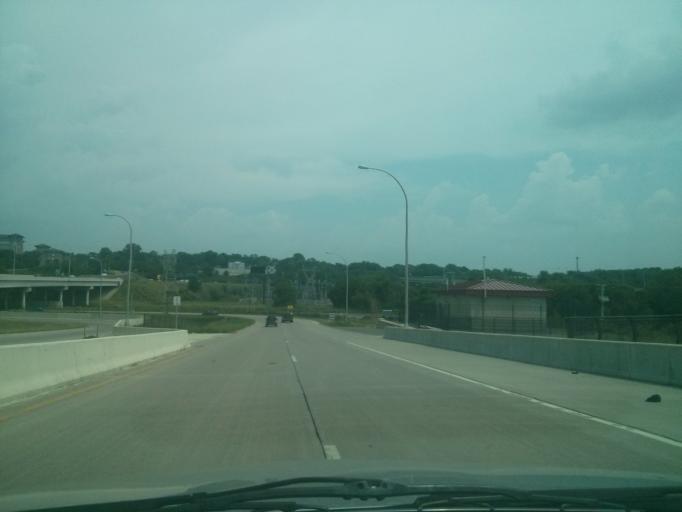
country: US
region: Minnesota
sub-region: Ramsey County
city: Saint Paul
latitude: 44.9529
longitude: -93.0805
